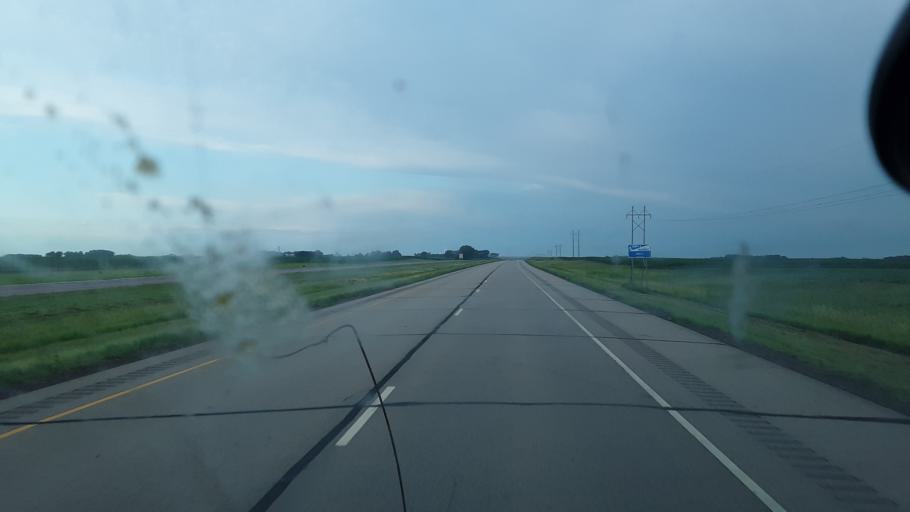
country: US
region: Minnesota
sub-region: Martin County
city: Fairmont
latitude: 43.6809
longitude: -94.5299
